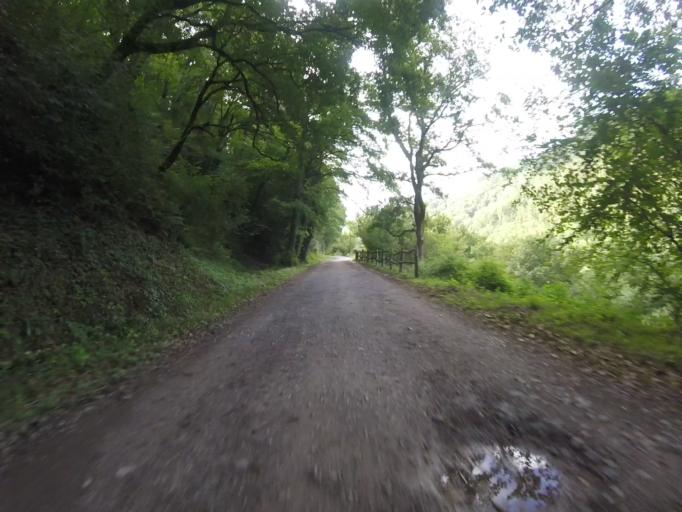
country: ES
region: Basque Country
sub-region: Provincia de Guipuzcoa
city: Andoain
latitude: 43.1964
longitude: -2.0100
